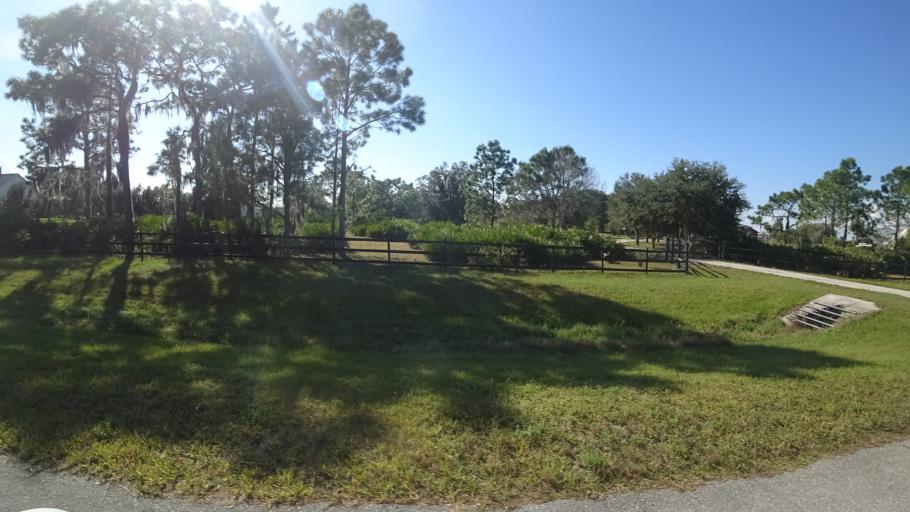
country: US
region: Florida
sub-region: Sarasota County
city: The Meadows
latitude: 27.4176
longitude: -82.2832
